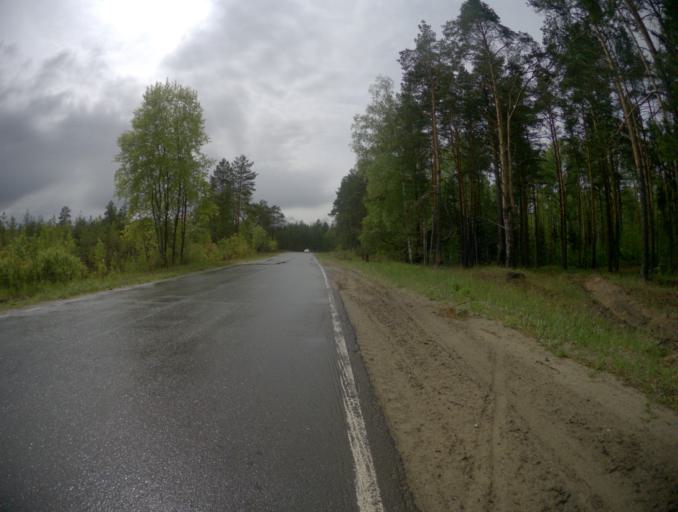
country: RU
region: Vladimir
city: Velikodvorskiy
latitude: 55.3743
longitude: 40.7837
